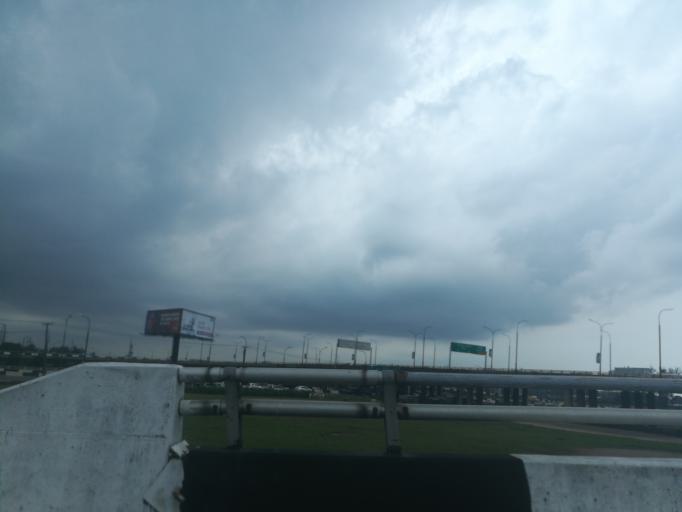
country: NG
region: Lagos
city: Lagos
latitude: 6.4562
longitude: 3.4065
